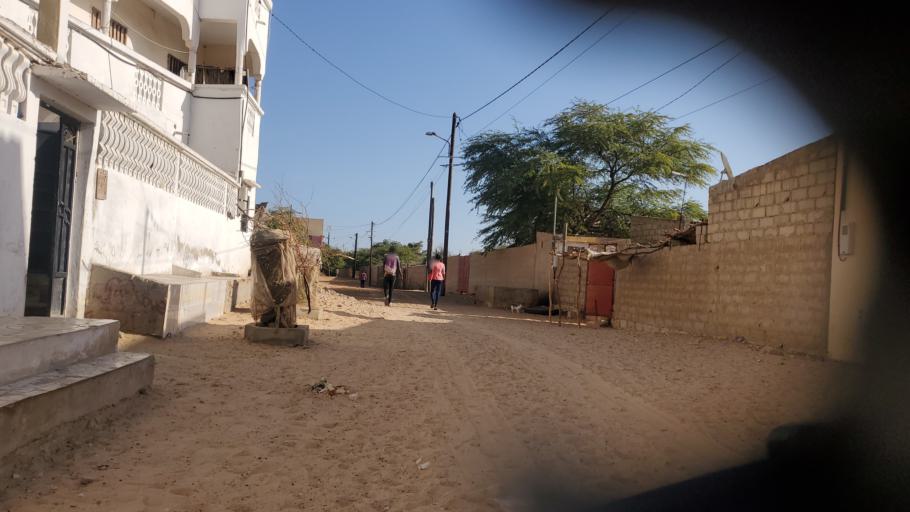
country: SN
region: Saint-Louis
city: Saint-Louis
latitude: 16.0583
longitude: -16.4216
